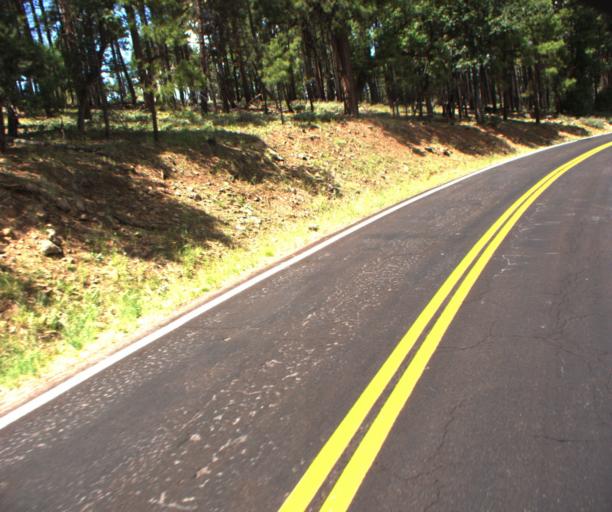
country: US
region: Arizona
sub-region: Greenlee County
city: Morenci
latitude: 33.4713
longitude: -109.3700
